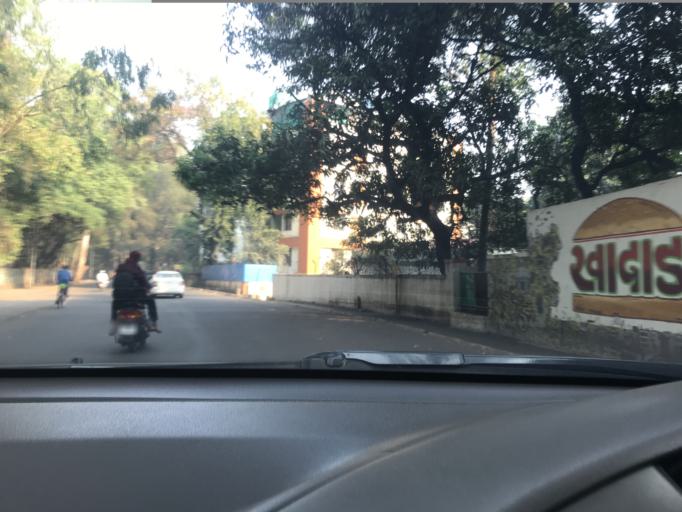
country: IN
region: Maharashtra
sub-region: Pune Division
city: Pune
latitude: 18.5085
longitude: 73.8287
